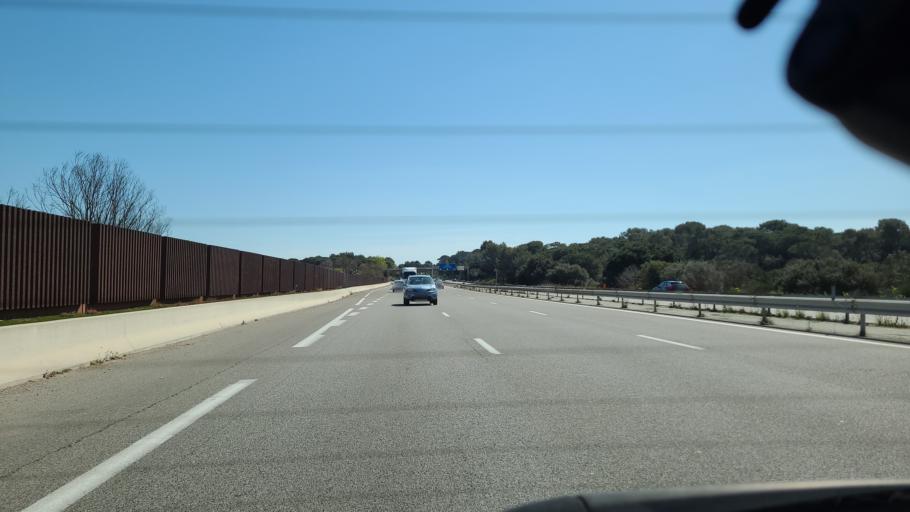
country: FR
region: Provence-Alpes-Cote d'Azur
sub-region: Departement du Var
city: Puget-sur-Argens
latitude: 43.4629
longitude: 6.6809
